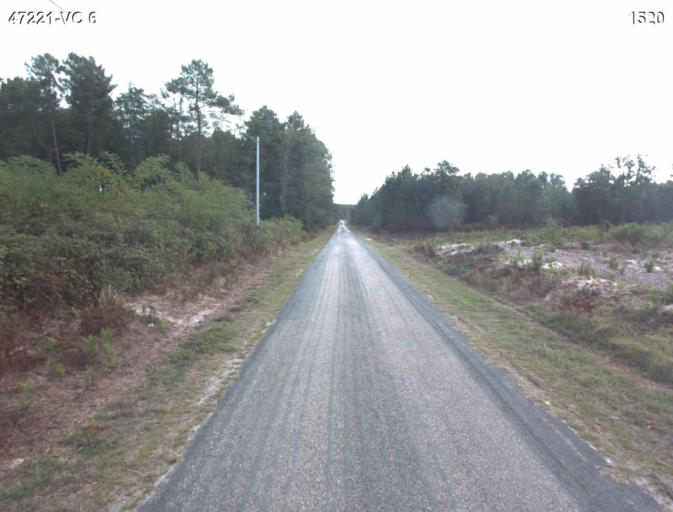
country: FR
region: Aquitaine
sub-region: Departement du Lot-et-Garonne
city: Mezin
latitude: 44.1035
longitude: 0.1631
